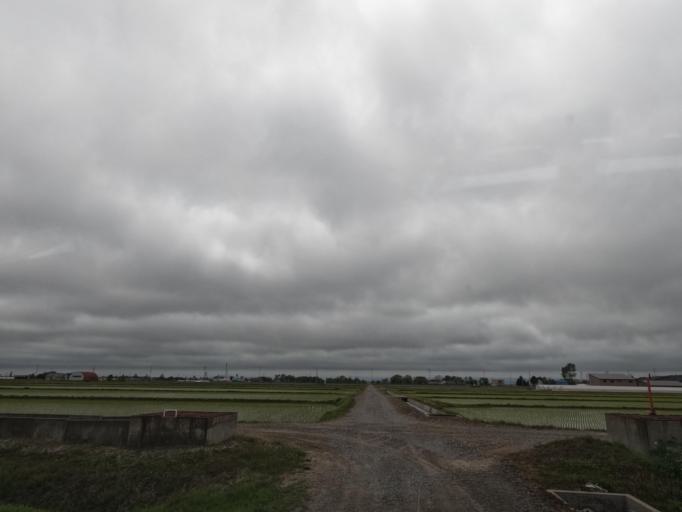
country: JP
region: Hokkaido
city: Tobetsu
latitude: 43.2465
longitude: 141.5195
